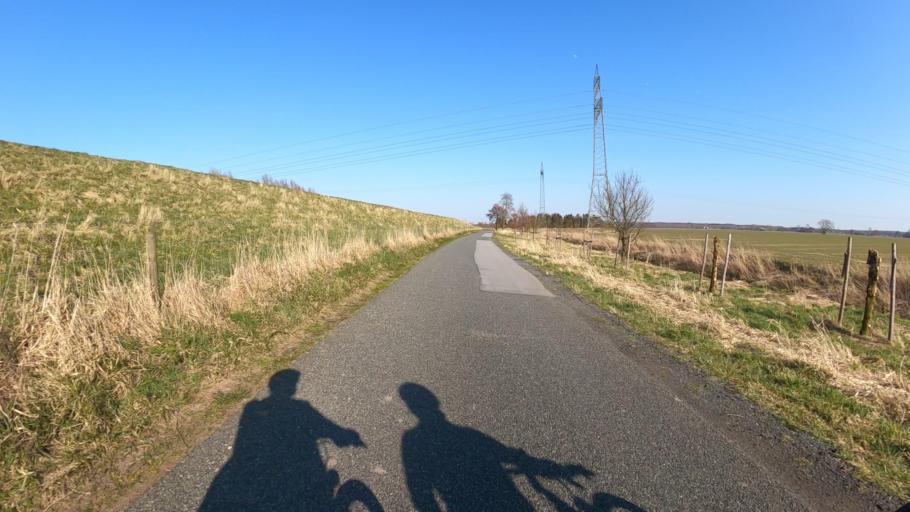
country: DE
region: Schleswig-Holstein
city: Seester
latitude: 53.7344
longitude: 9.6070
